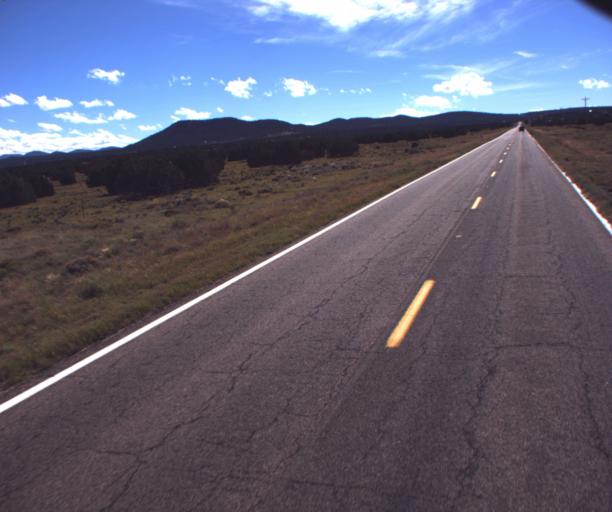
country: US
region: Arizona
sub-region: Navajo County
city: White Mountain Lake
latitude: 34.3431
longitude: -109.7299
